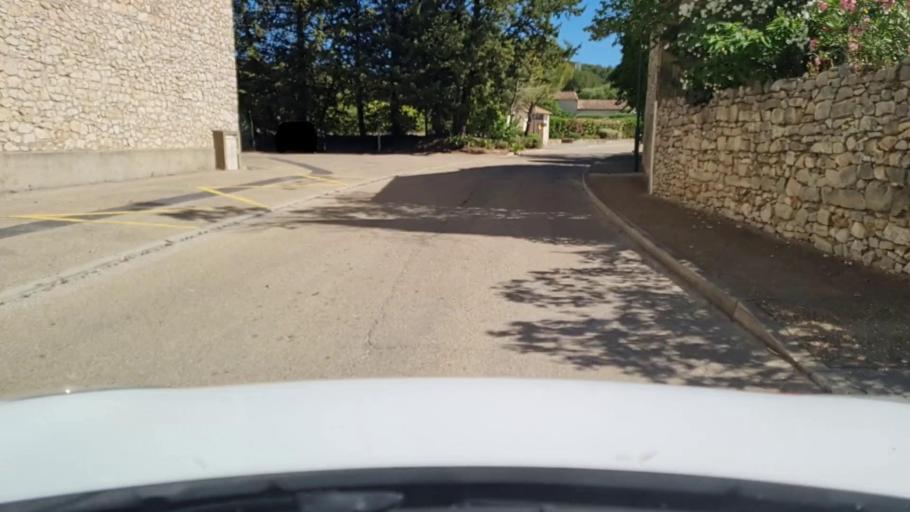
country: FR
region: Languedoc-Roussillon
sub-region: Departement du Gard
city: Villevieille
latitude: 43.8580
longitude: 4.1147
